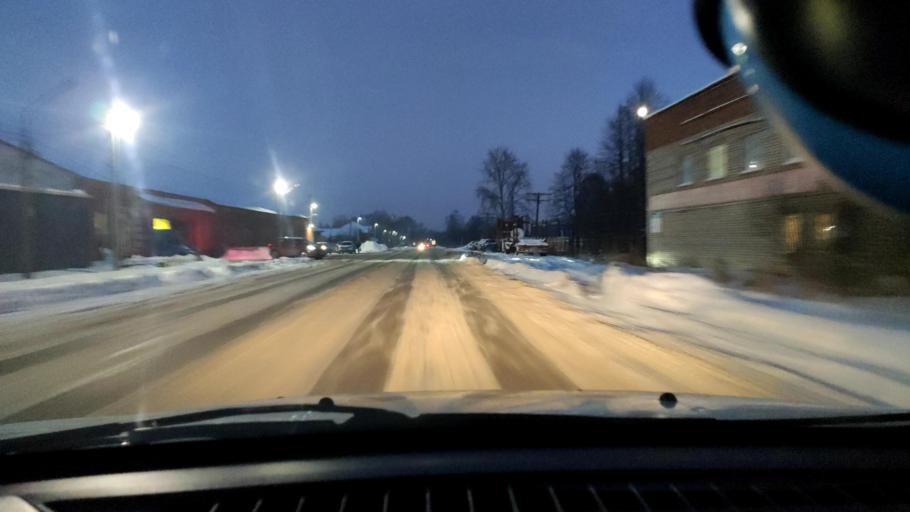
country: RU
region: Perm
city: Kultayevo
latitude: 57.8905
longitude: 55.9289
